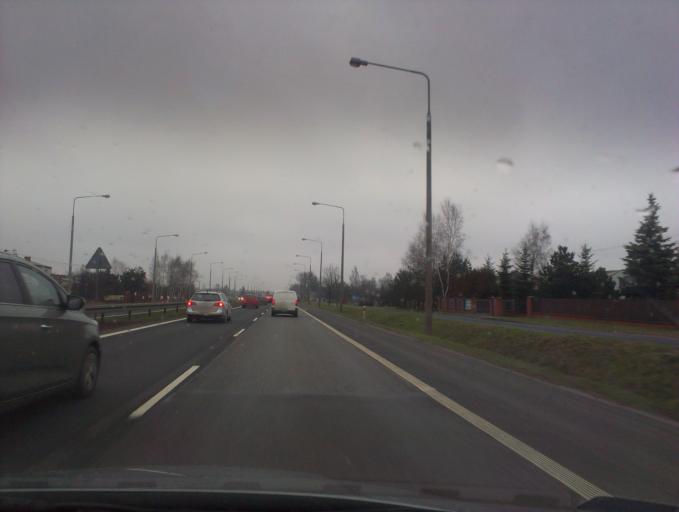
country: PL
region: Masovian Voivodeship
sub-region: Powiat radomski
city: Jedlinsk
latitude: 51.4778
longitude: 21.1298
